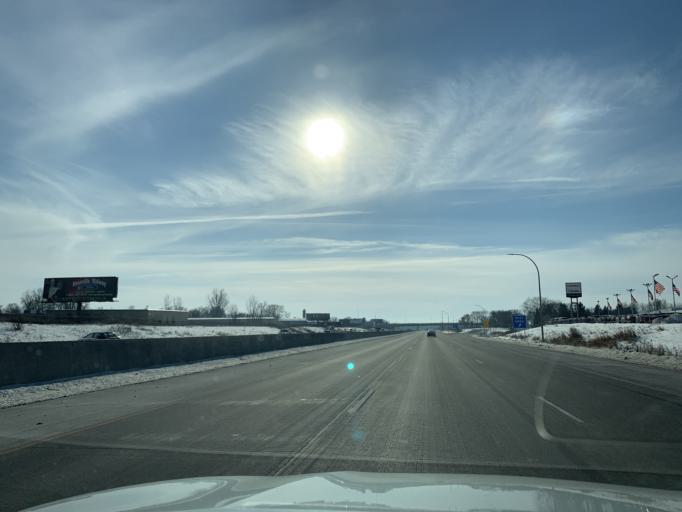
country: US
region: Minnesota
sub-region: Washington County
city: Forest Lake
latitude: 45.2744
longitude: -93.0059
